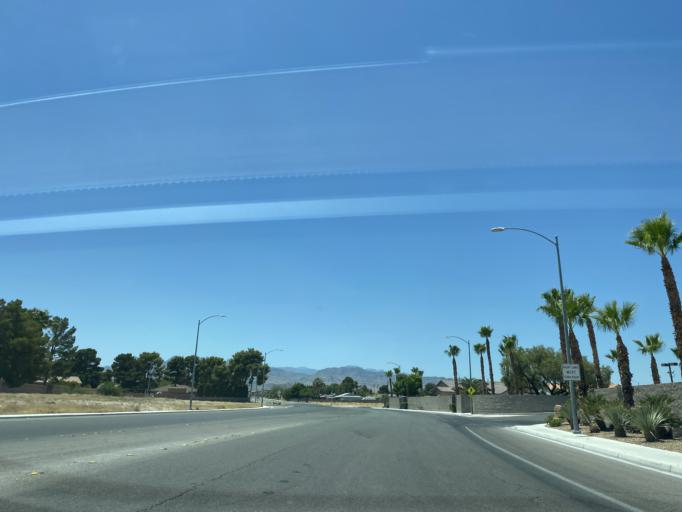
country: US
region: Nevada
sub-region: Clark County
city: Las Vegas
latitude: 36.2317
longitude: -115.2149
